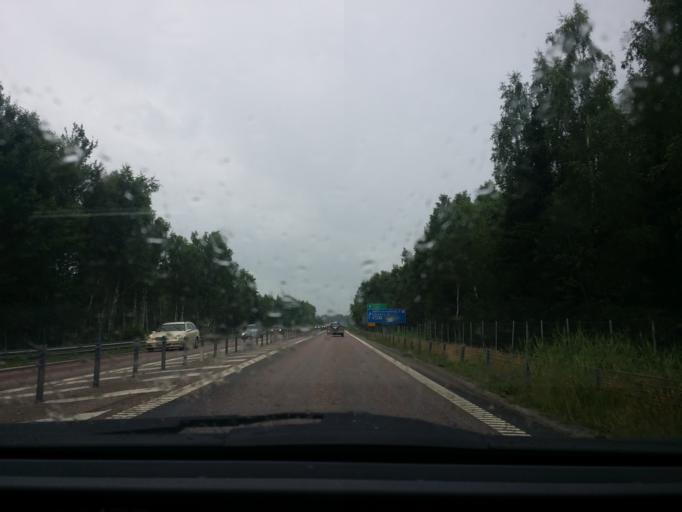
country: SE
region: Vaestmanland
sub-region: Hallstahammars Kommun
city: Kolback
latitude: 59.5867
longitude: 16.2730
